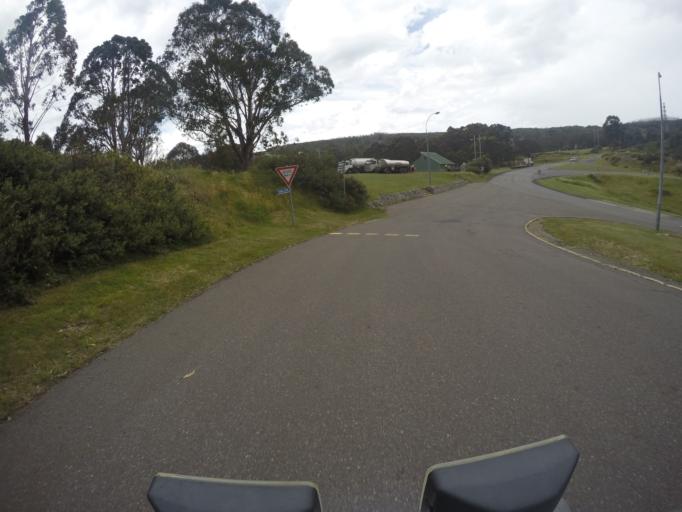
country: AU
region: New South Wales
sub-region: Snowy River
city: Jindabyne
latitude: -35.9359
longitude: 148.3829
